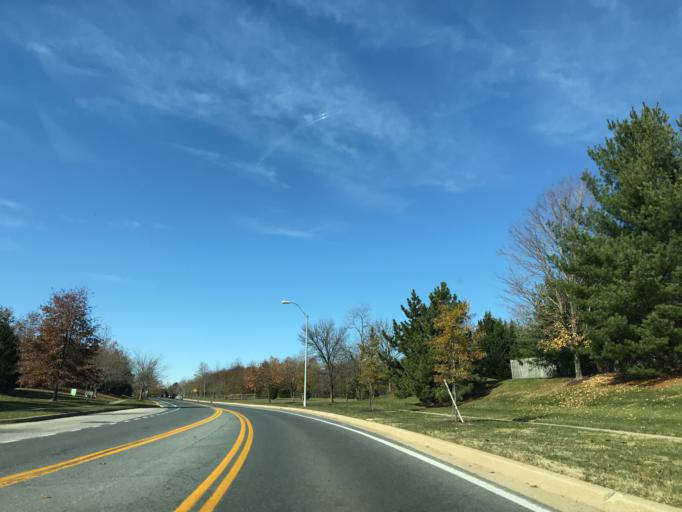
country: US
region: Maryland
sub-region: Howard County
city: Ilchester
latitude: 39.2115
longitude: -76.7776
